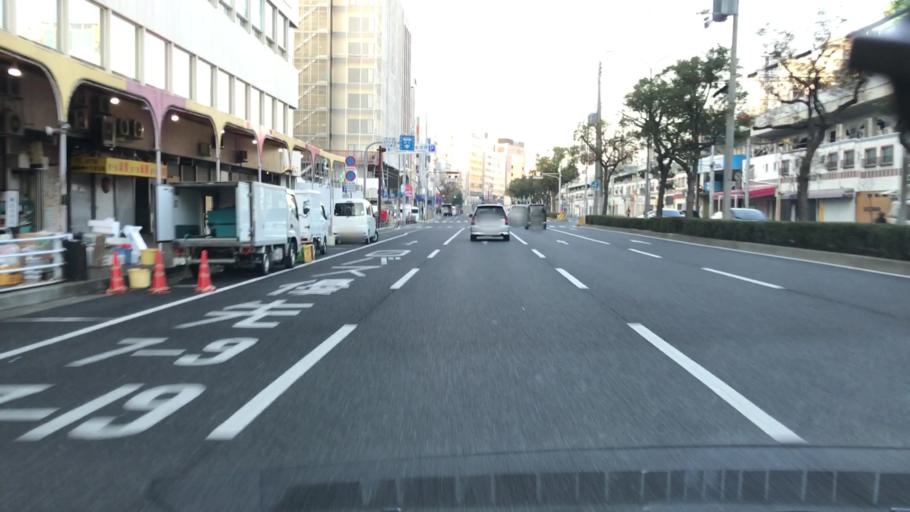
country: JP
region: Hyogo
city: Kobe
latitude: 34.6913
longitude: 135.1910
